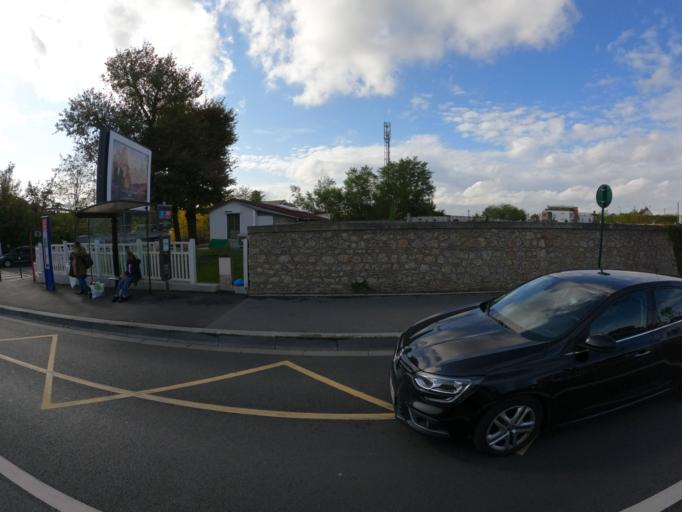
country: FR
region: Ile-de-France
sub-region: Departement de Seine-et-Marne
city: Vaires-sur-Marne
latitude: 48.8759
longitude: 2.6386
